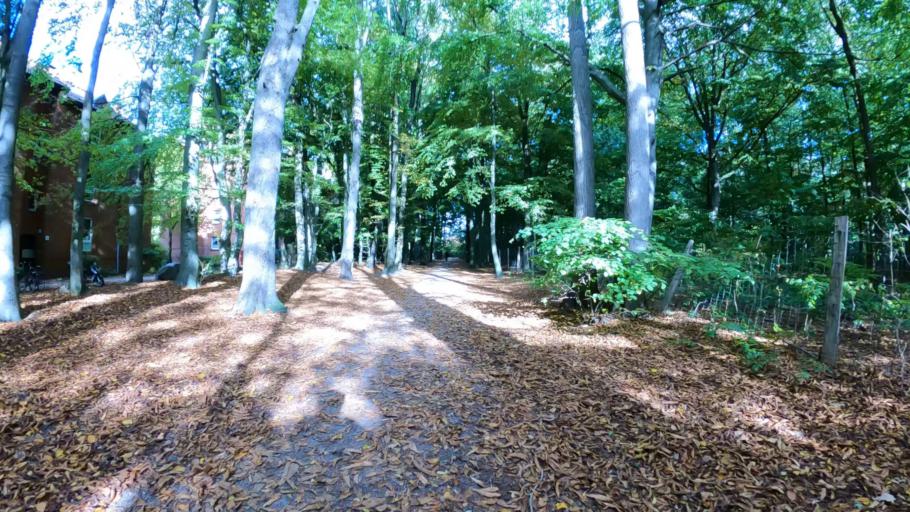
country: DE
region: Schleswig-Holstein
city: Delingsdorf
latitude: 53.6874
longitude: 10.2481
